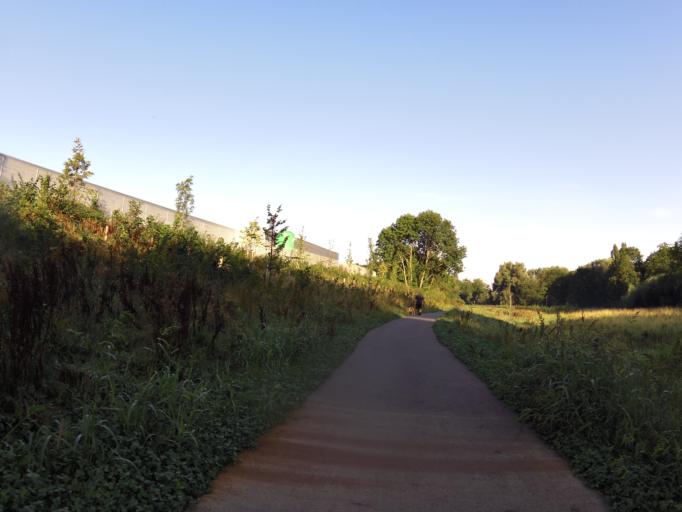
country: NL
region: Limburg
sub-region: Gemeente Heerlen
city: Heerlen
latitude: 50.9040
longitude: 5.9611
